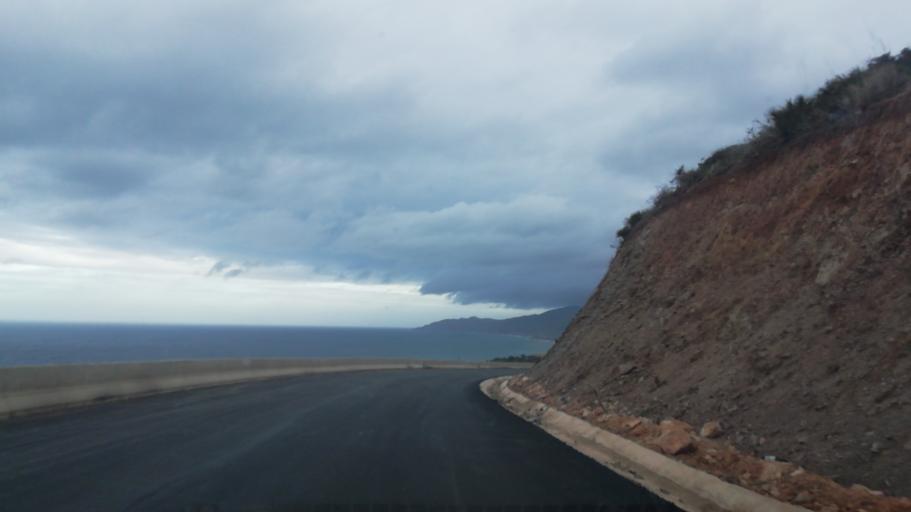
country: DZ
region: Oran
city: Bir el Djir
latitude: 35.7705
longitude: -0.5174
